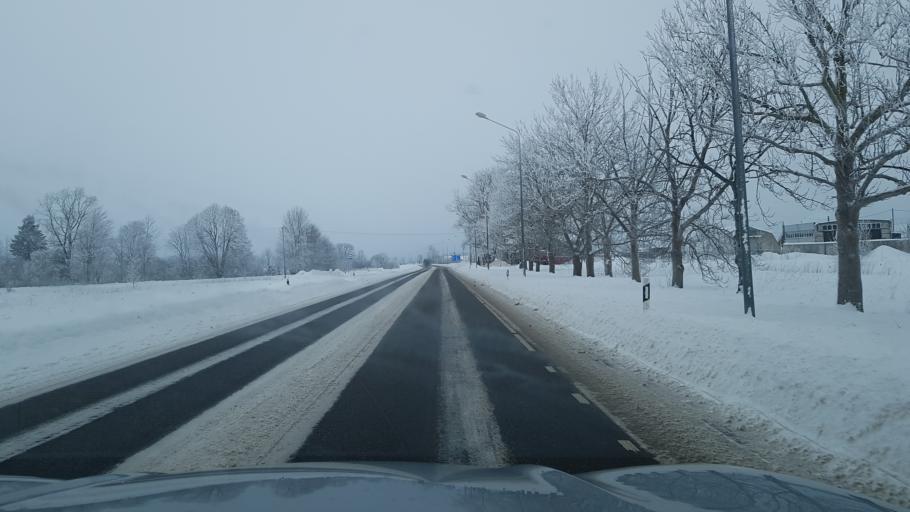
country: EE
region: Ida-Virumaa
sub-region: Johvi vald
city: Johvi
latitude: 59.3316
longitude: 27.4029
